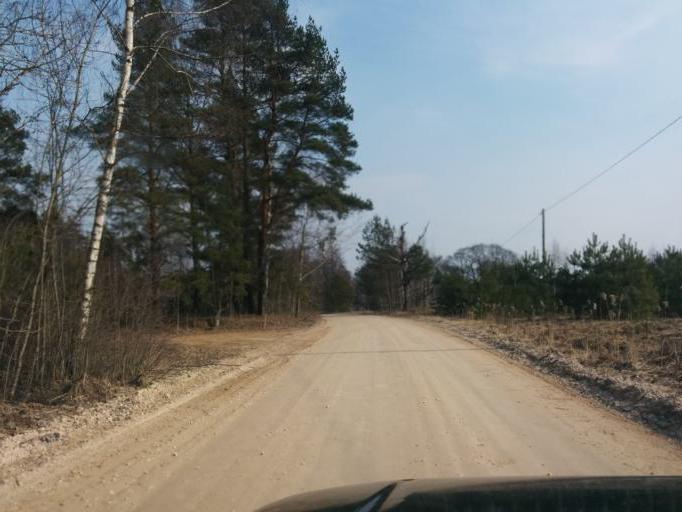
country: LV
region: Olaine
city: Olaine
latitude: 56.7901
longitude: 24.0070
